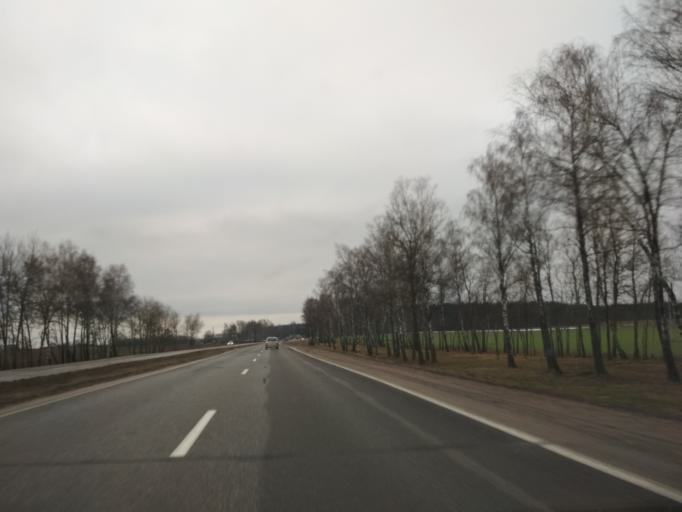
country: BY
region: Minsk
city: Luhavaya Slabada
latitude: 53.7802
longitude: 27.8246
